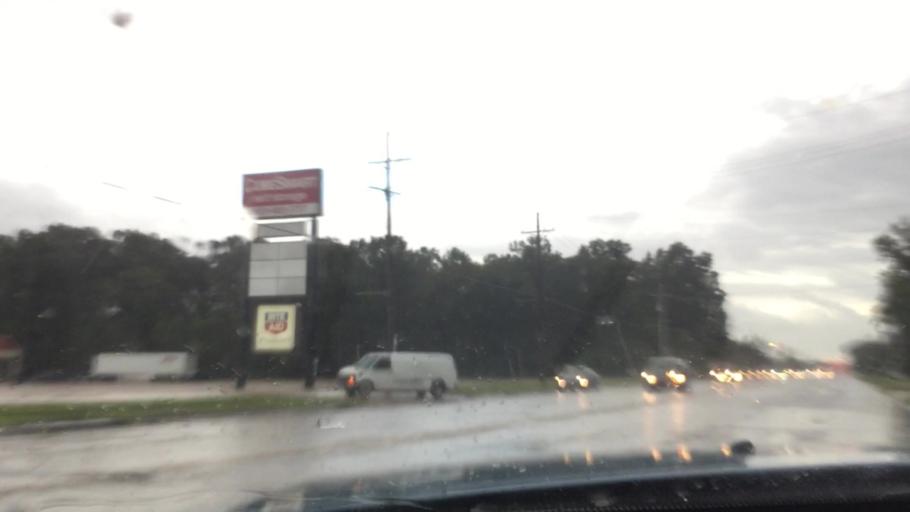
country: US
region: Louisiana
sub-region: East Baton Rouge Parish
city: Monticello
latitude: 30.4513
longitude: -91.0246
